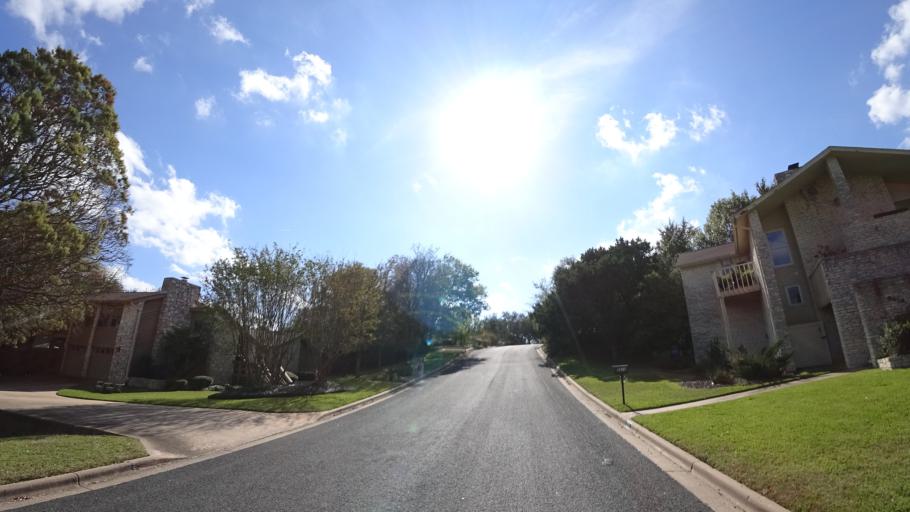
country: US
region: Texas
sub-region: Williamson County
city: Anderson Mill
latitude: 30.4285
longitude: -97.8035
